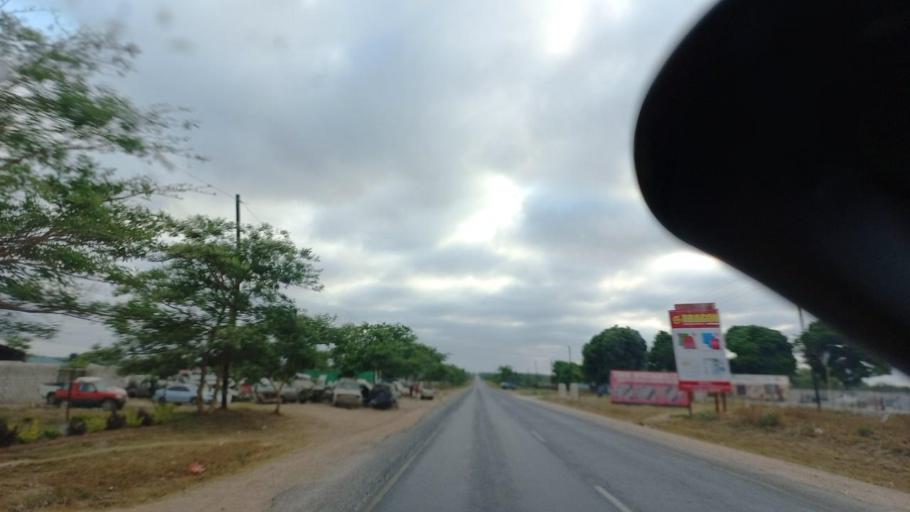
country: ZM
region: Lusaka
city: Chongwe
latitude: -15.3531
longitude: 28.4884
